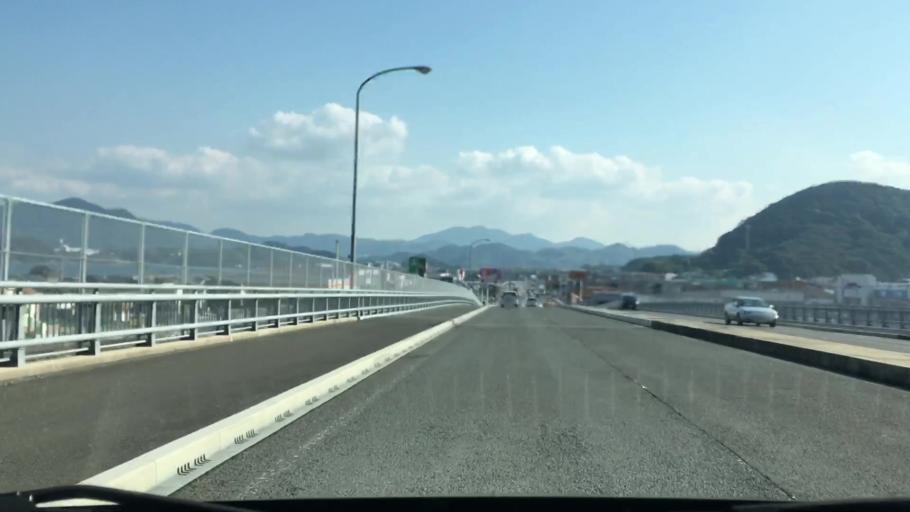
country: JP
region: Nagasaki
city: Togitsu
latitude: 32.8542
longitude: 129.8230
